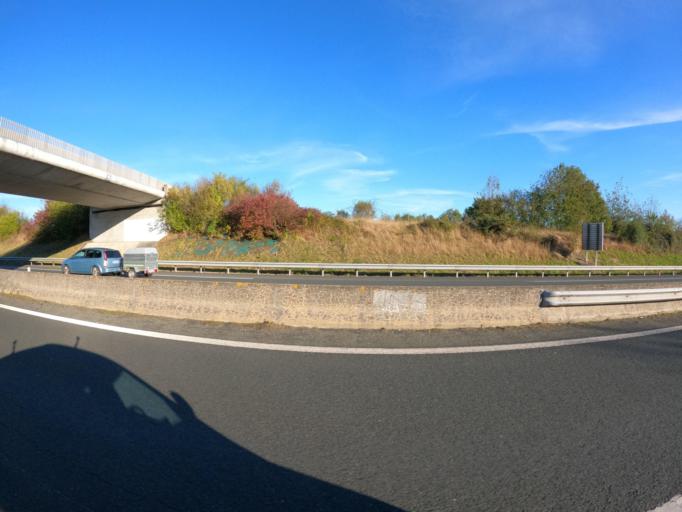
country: FR
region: Pays de la Loire
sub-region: Departement de Maine-et-Loire
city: Mazieres-en-Mauges
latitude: 47.0568
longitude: -0.8321
